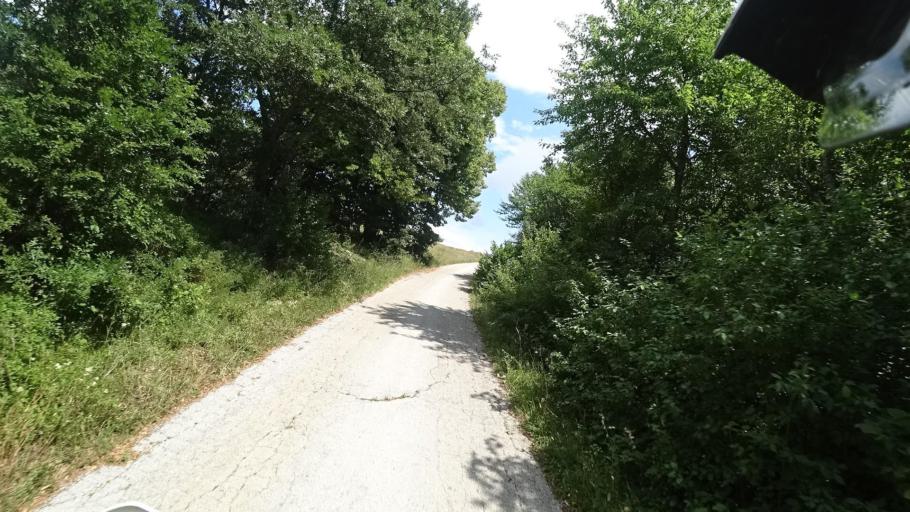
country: HR
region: Licko-Senjska
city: Jezerce
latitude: 44.6171
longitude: 15.6383
